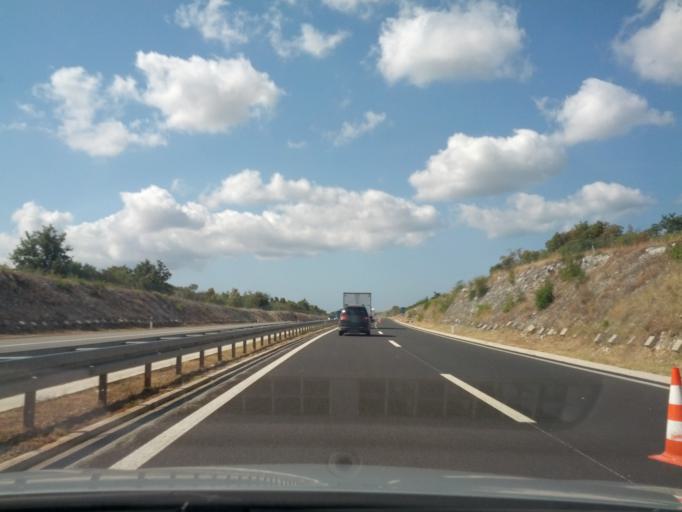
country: HR
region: Istarska
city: Vodnjan
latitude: 45.0168
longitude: 13.8416
